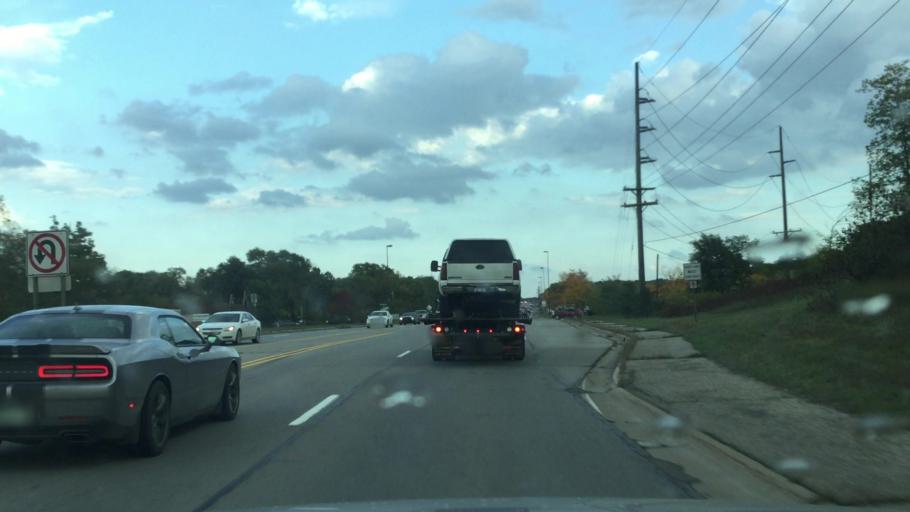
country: US
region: Michigan
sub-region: Oakland County
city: Milford
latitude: 42.6535
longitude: -83.5856
